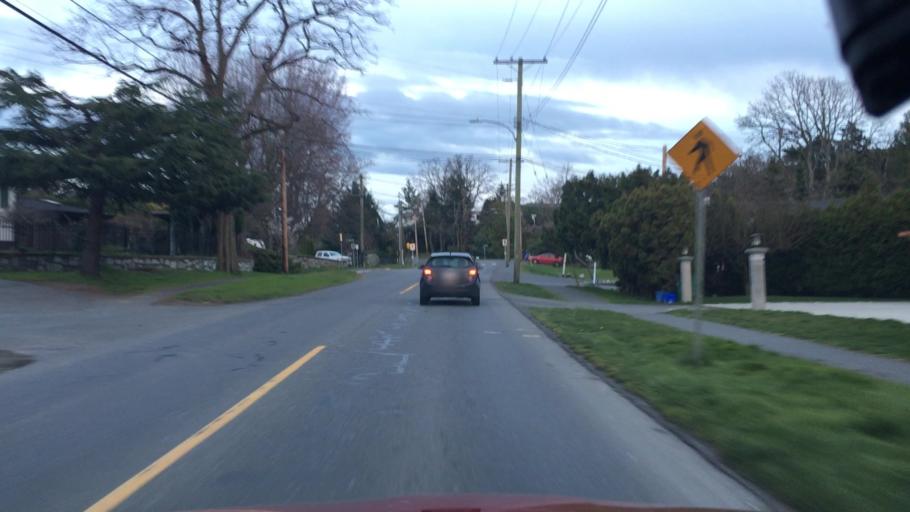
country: CA
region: British Columbia
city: Victoria
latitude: 48.4646
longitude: -123.3433
